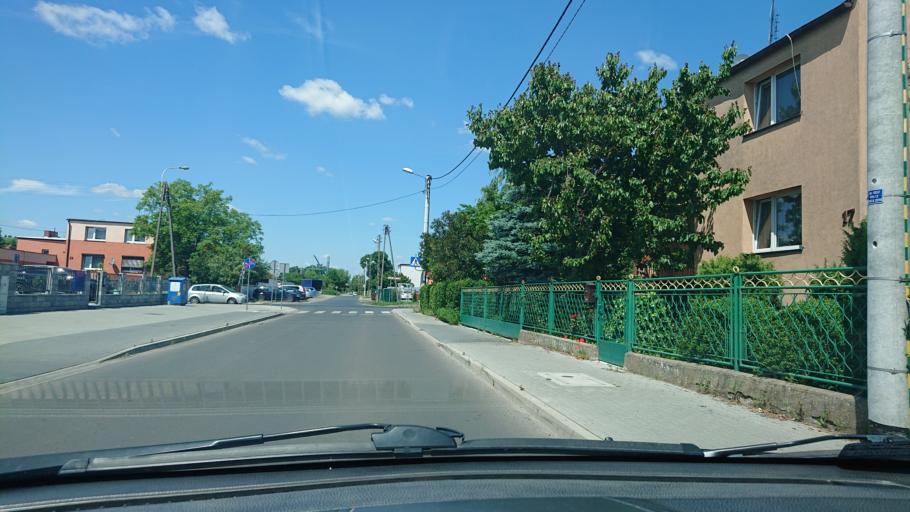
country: PL
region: Greater Poland Voivodeship
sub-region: Powiat gnieznienski
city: Gniezno
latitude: 52.5226
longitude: 17.6115
